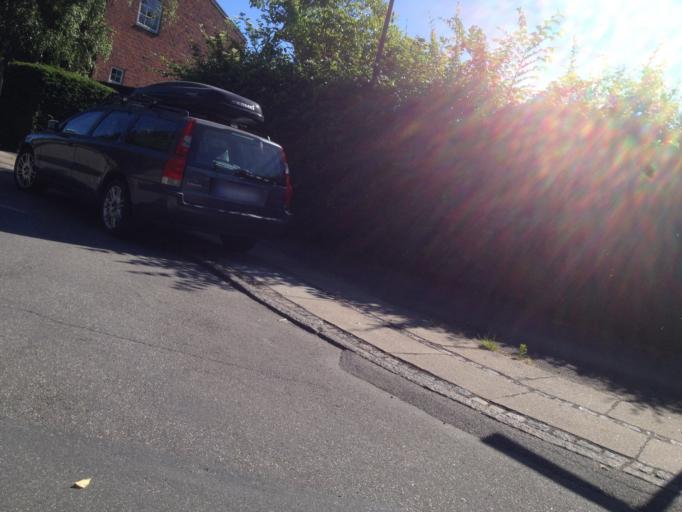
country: DK
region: Capital Region
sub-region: Gentofte Kommune
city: Charlottenlund
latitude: 55.7473
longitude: 12.5742
